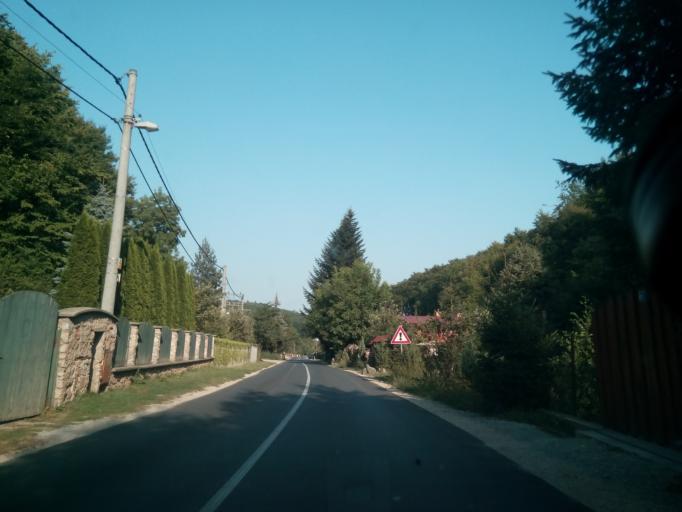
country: SK
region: Kosicky
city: Kosice
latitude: 48.7238
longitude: 21.1595
